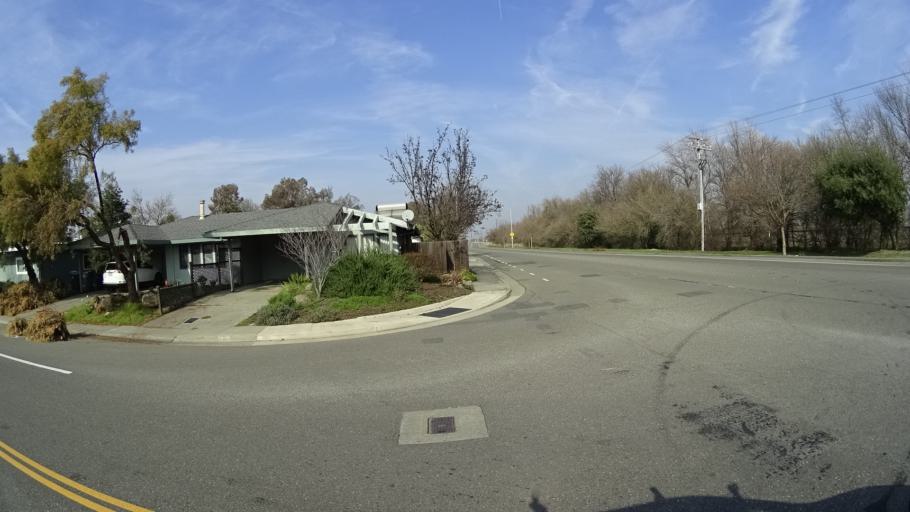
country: US
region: California
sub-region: Yolo County
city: Davis
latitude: 38.5695
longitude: -121.7464
